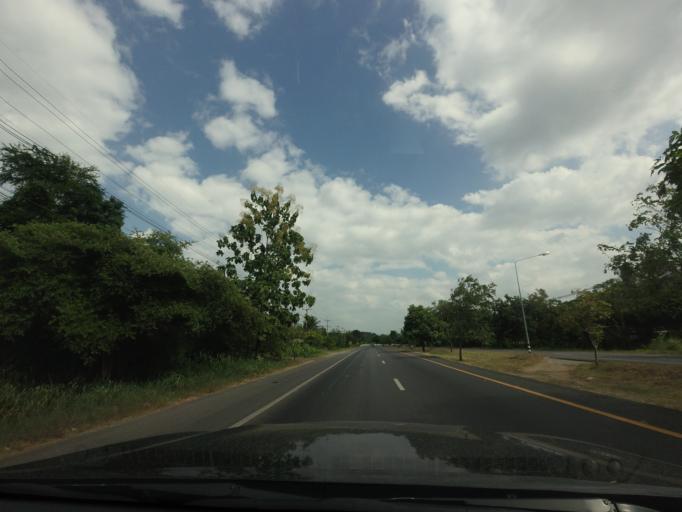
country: TH
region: Lop Buri
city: Chai Badan
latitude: 15.3005
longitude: 101.1270
